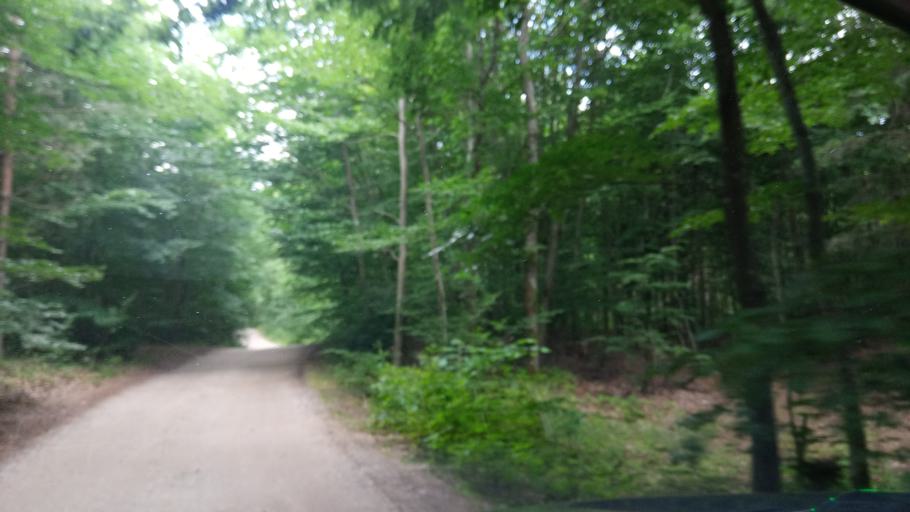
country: PL
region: West Pomeranian Voivodeship
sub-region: Powiat szczecinecki
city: Szczecinek
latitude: 53.7024
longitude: 16.6679
